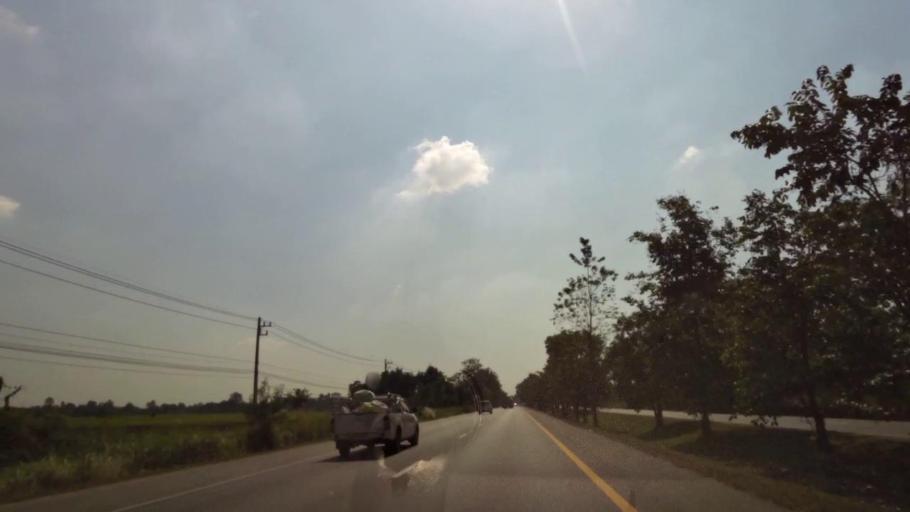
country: TH
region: Phichit
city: Bueng Na Rang
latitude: 16.1662
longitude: 100.1266
